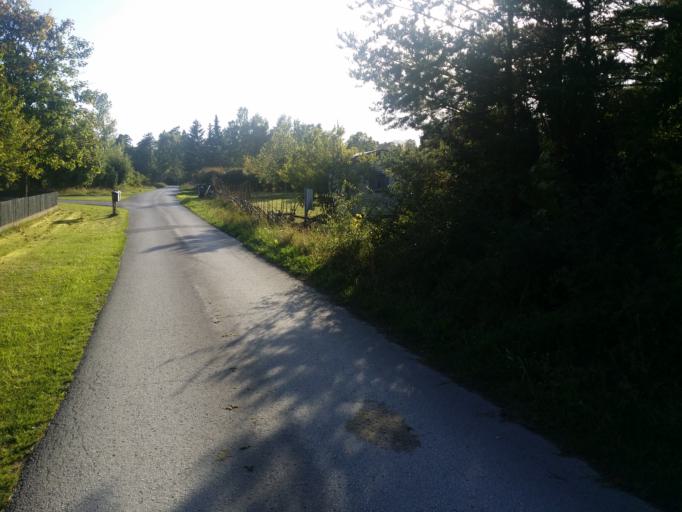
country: SE
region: Gotland
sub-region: Gotland
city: Klintehamn
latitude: 57.4838
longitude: 18.1376
